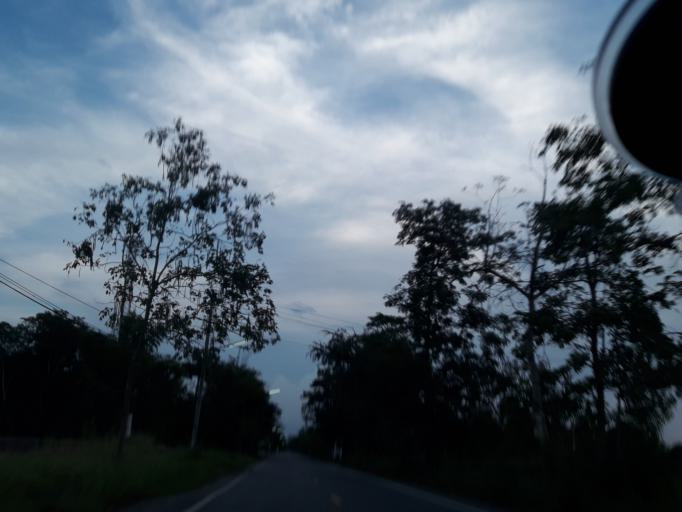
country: TH
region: Pathum Thani
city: Nong Suea
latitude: 14.1668
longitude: 100.8690
